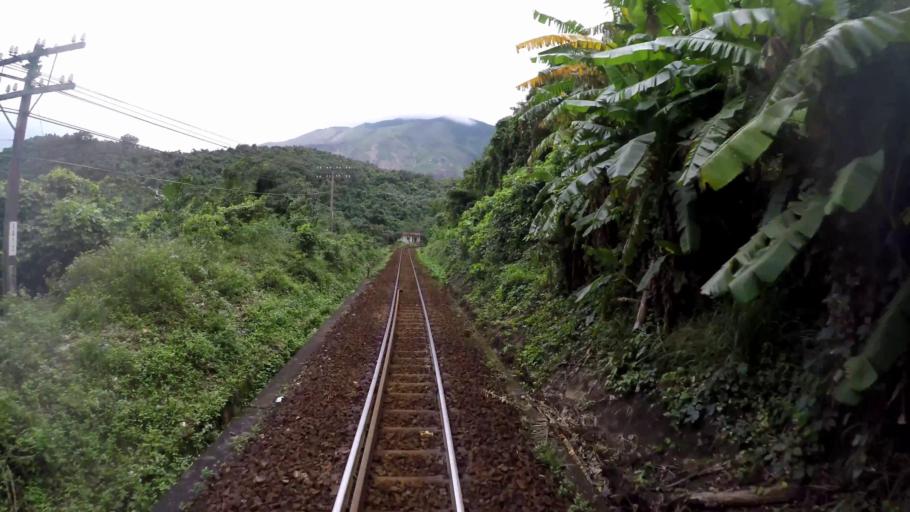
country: VN
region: Da Nang
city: Lien Chieu
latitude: 16.1716
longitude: 108.1453
